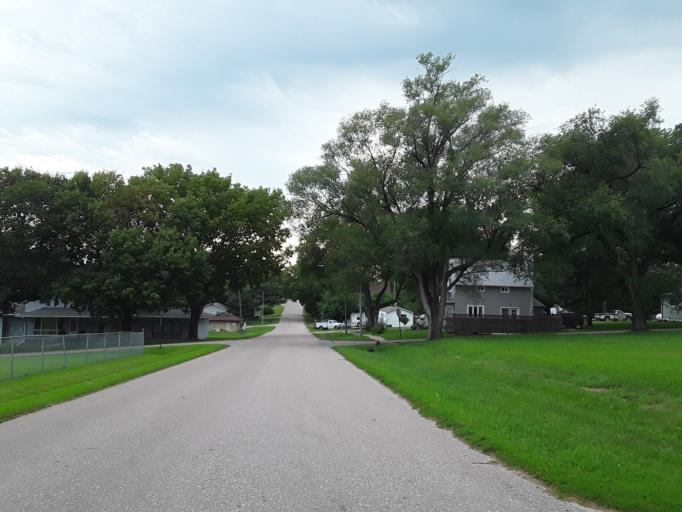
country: US
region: Nebraska
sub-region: Saunders County
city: Ashland
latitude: 41.0952
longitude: -96.4316
